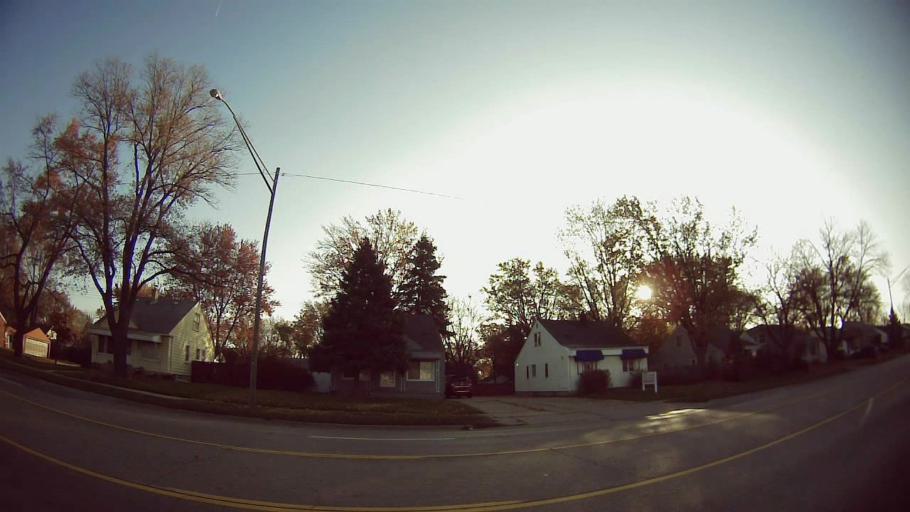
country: US
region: Michigan
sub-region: Oakland County
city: Lathrup Village
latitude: 42.4906
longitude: -83.2026
